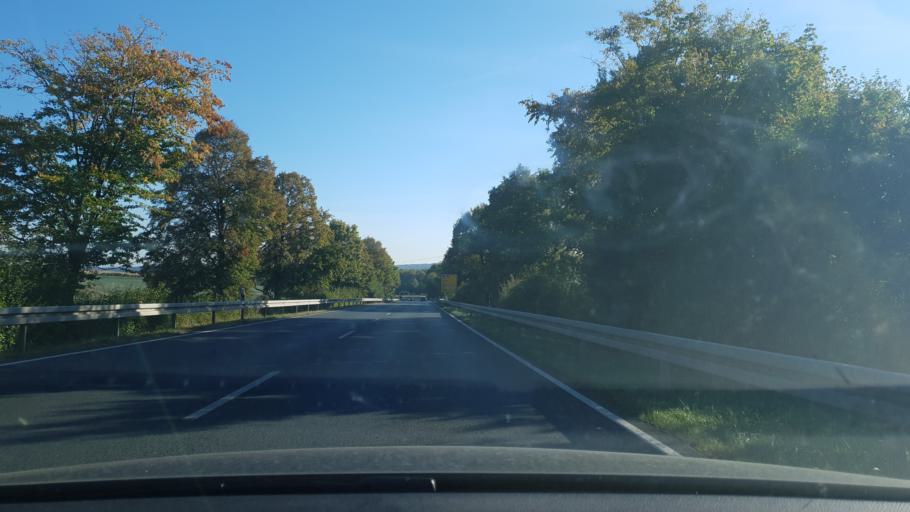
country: DE
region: Hesse
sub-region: Regierungsbezirk Giessen
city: Langgons
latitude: 50.4744
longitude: 8.6493
